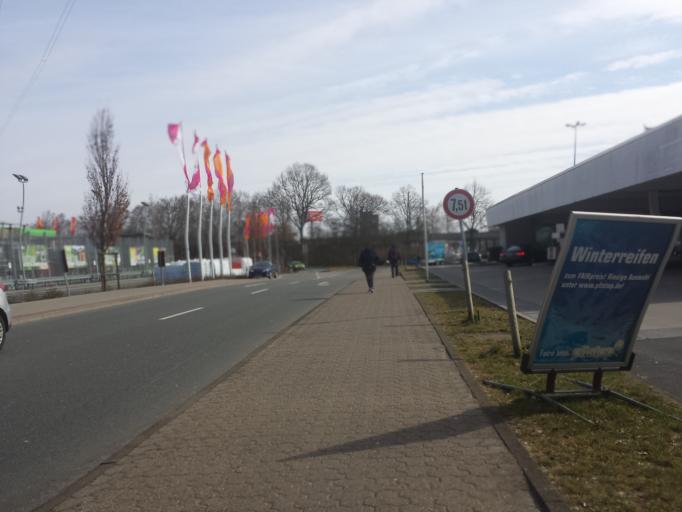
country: DE
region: Lower Saxony
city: Stuhr
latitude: 53.0636
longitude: 8.7717
